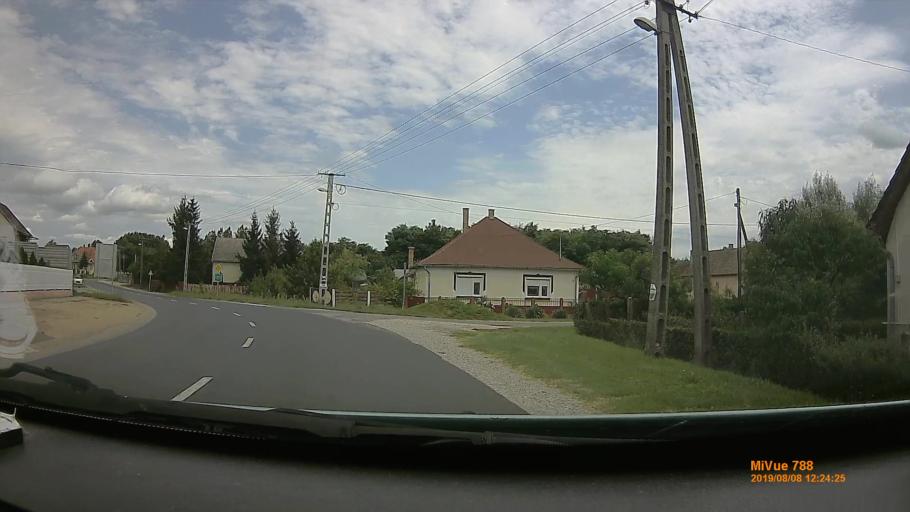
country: HU
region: Szabolcs-Szatmar-Bereg
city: Nyirbogat
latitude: 47.8045
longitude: 22.0646
